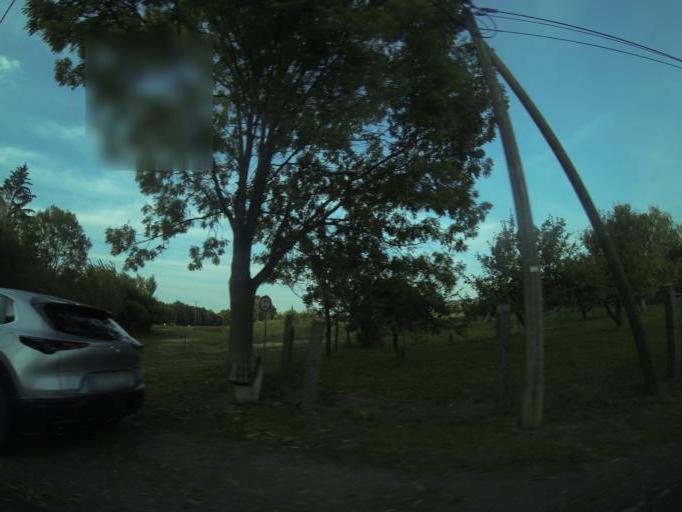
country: DE
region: Thuringia
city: Altkirchen
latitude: 50.9256
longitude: 12.3406
